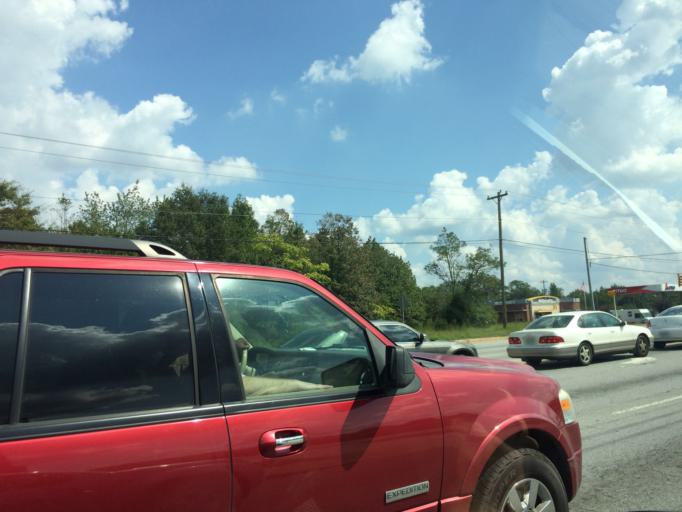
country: US
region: South Carolina
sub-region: Greenville County
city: Gantt
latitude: 34.7954
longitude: -82.4201
